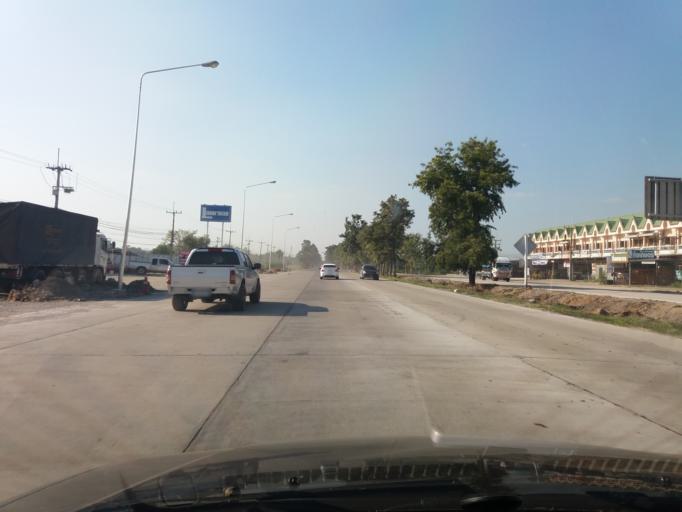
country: TH
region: Nakhon Sawan
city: Kao Liao
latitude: 15.7717
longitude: 99.9837
